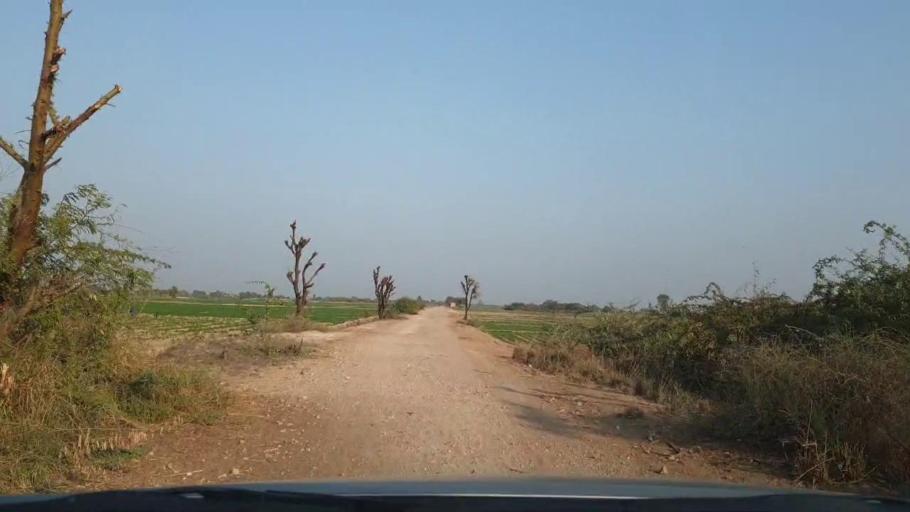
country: PK
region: Sindh
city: Tando Adam
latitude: 25.6864
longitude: 68.6328
